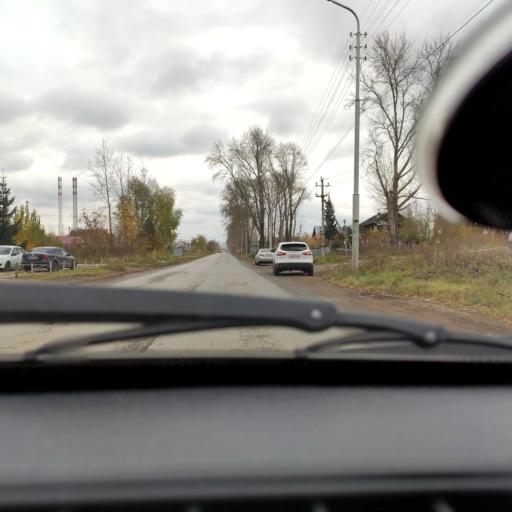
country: RU
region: Bashkortostan
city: Mikhaylovka
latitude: 54.7747
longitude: 55.8925
